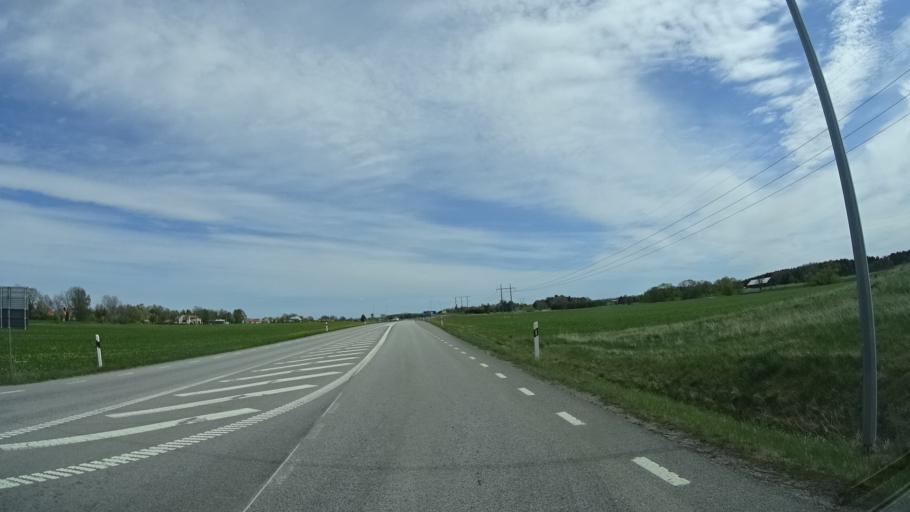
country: SE
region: OEstergoetland
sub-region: Linkopings Kommun
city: Vikingstad
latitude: 58.3763
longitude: 15.4280
